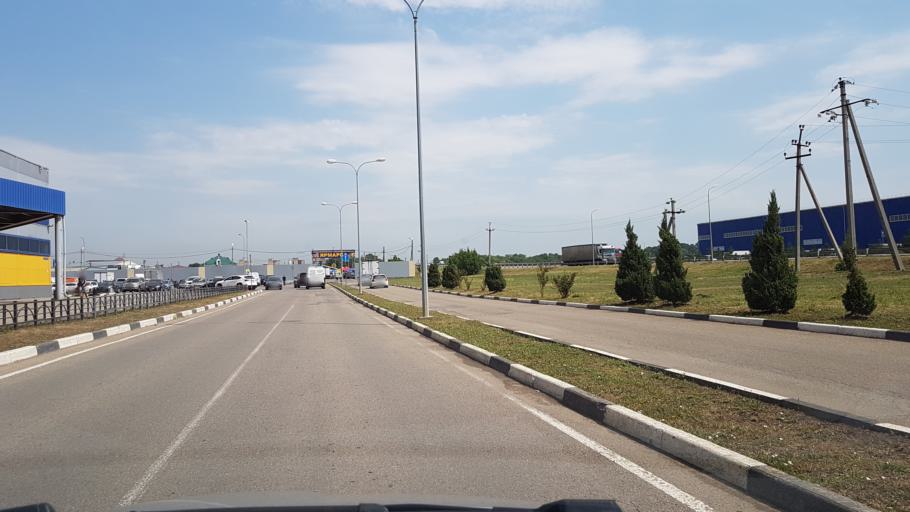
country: RU
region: Krasnodarskiy
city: Pashkovskiy
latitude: 45.0377
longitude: 39.1275
